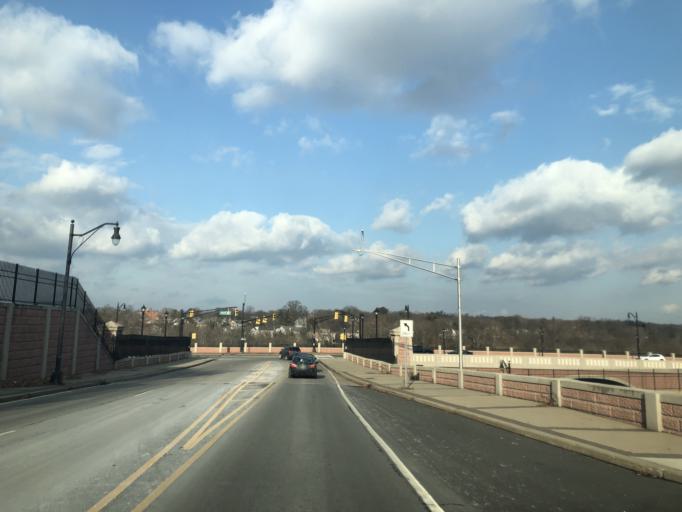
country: US
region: New Jersey
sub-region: Middlesex County
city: Highland Park
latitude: 40.4861
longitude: -74.4327
